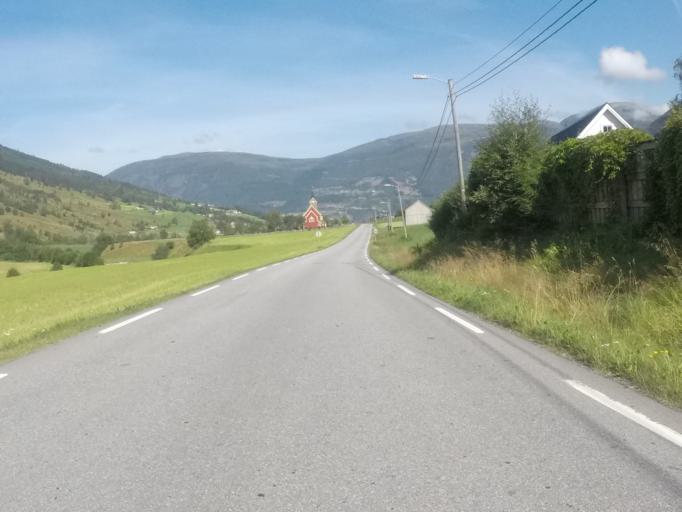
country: NO
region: Sogn og Fjordane
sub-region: Stryn
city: Stryn
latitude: 61.8242
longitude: 6.8095
